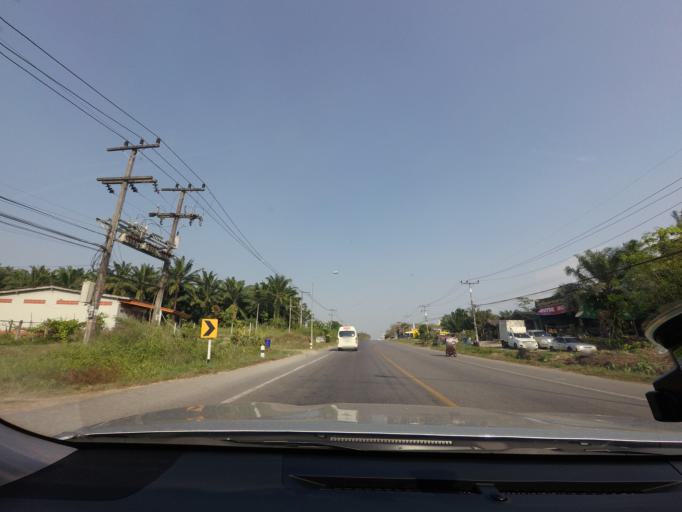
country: TH
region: Surat Thani
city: Phrasaeng
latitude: 8.5737
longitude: 99.2200
